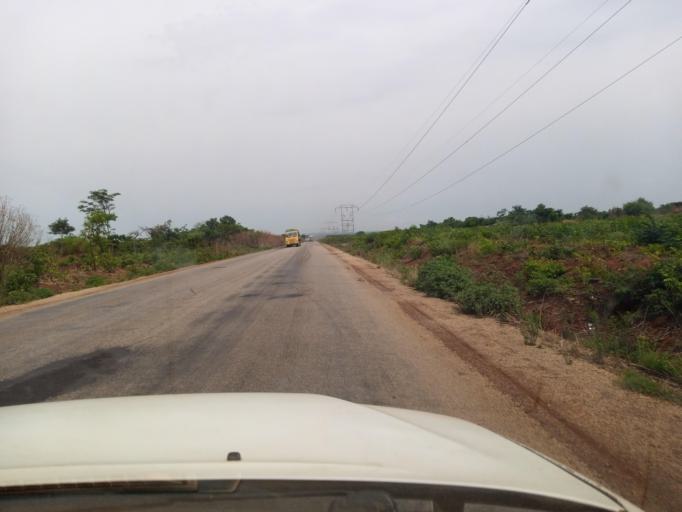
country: CD
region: Katanga
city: Likasi
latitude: -11.0670
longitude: 26.9801
